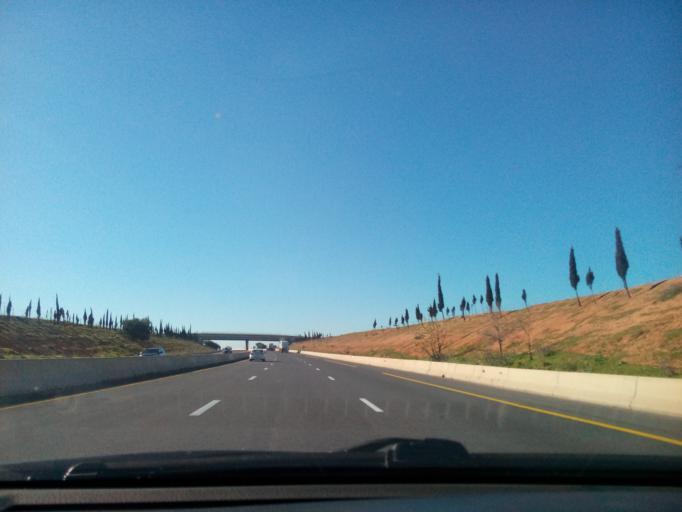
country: DZ
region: Relizane
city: Djidiouia
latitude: 35.8989
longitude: 0.7139
